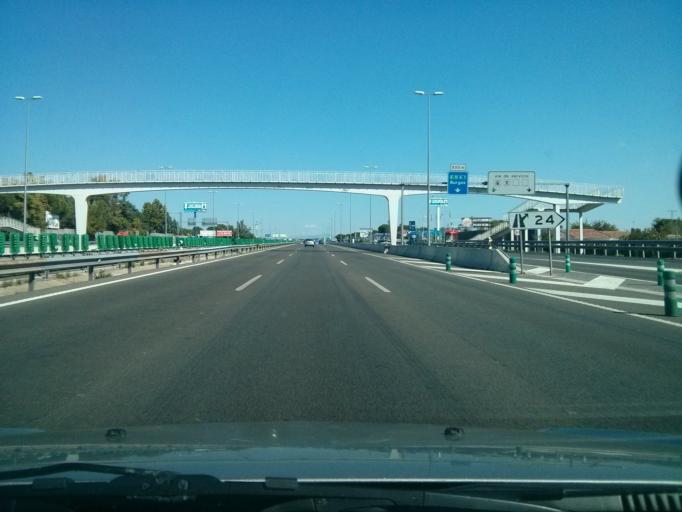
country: ES
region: Madrid
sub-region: Provincia de Madrid
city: San Sebastian de los Reyes
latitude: 40.5877
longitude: -3.5833
